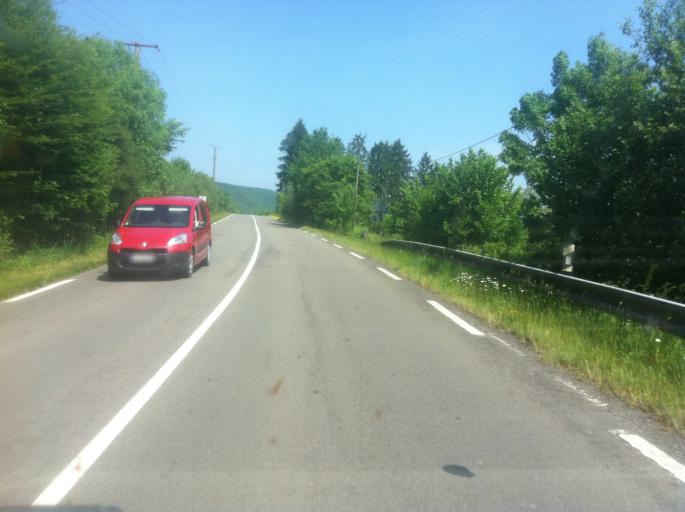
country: FR
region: Champagne-Ardenne
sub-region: Departement des Ardennes
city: Haybes
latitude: 50.0348
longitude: 4.7259
